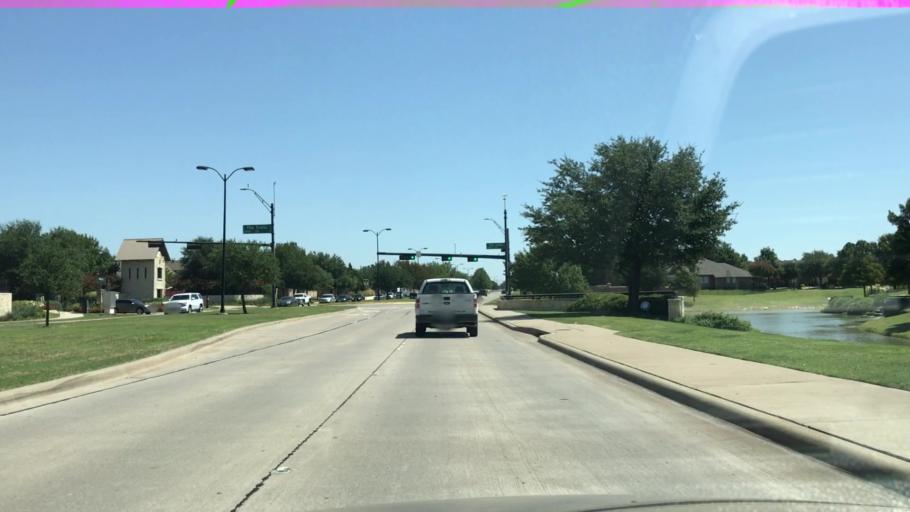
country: US
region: Texas
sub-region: Collin County
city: Frisco
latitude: 33.1531
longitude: -96.8730
